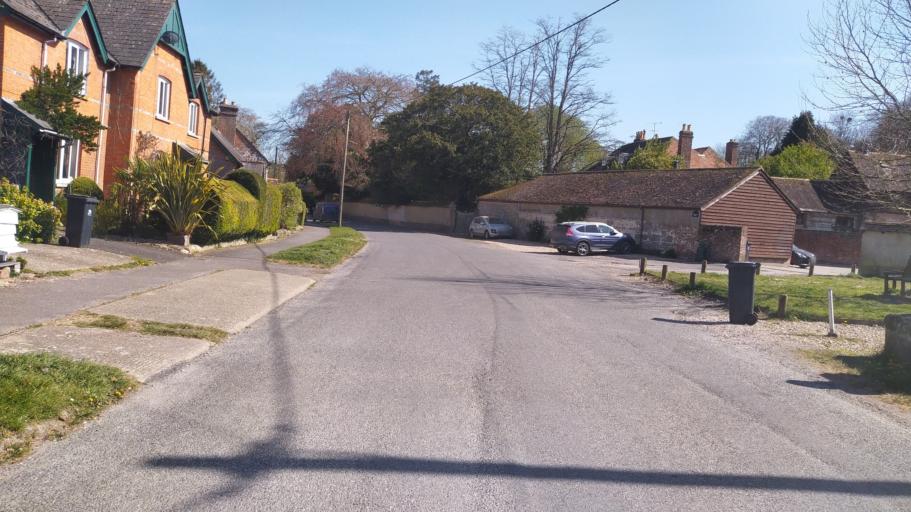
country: GB
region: England
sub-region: Dorset
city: Blandford Forum
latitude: 50.8844
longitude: -2.1375
